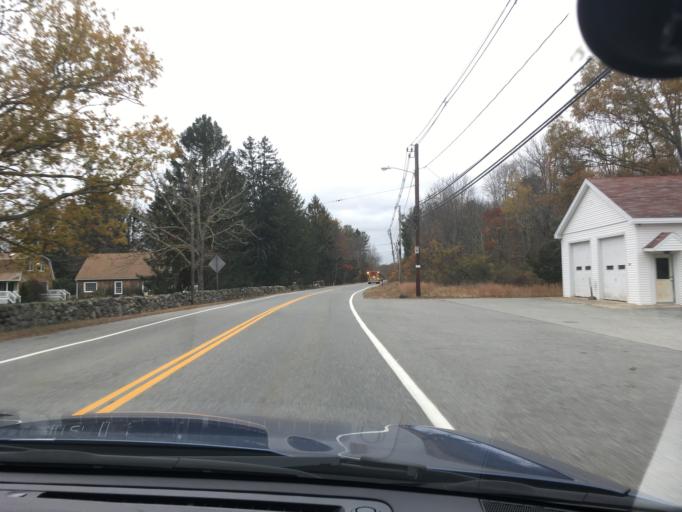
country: US
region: Rhode Island
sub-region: Providence County
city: North Scituate
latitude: 41.8154
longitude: -71.6629
